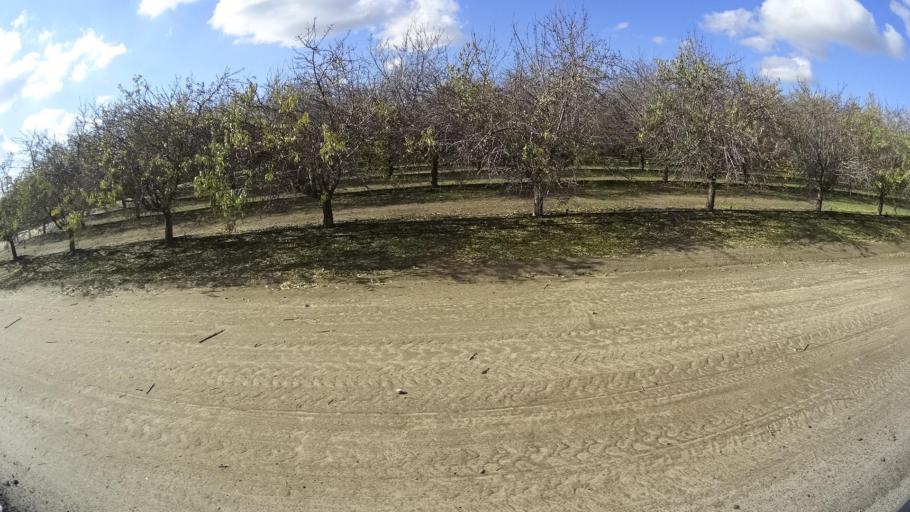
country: US
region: California
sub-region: Kern County
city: Delano
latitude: 35.7437
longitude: -119.3478
